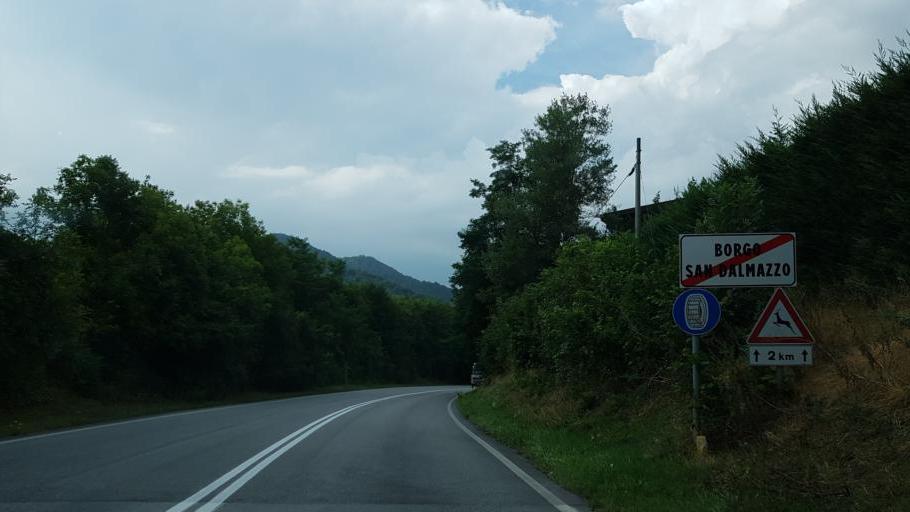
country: IT
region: Piedmont
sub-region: Provincia di Cuneo
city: Borgo San Dalmazzo
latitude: 44.3394
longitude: 7.4768
